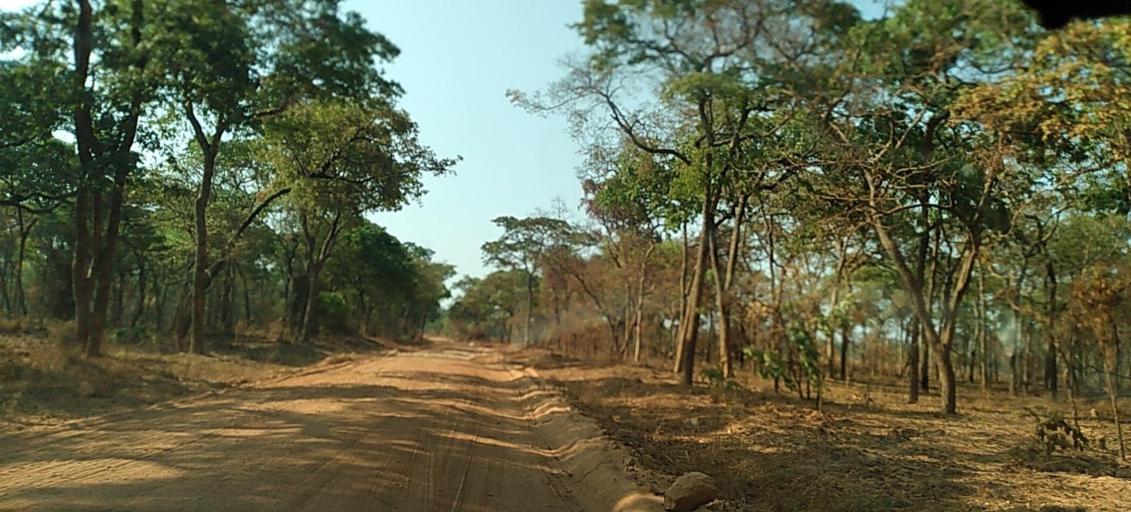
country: ZM
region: North-Western
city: Kasempa
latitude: -13.6799
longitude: 26.0230
